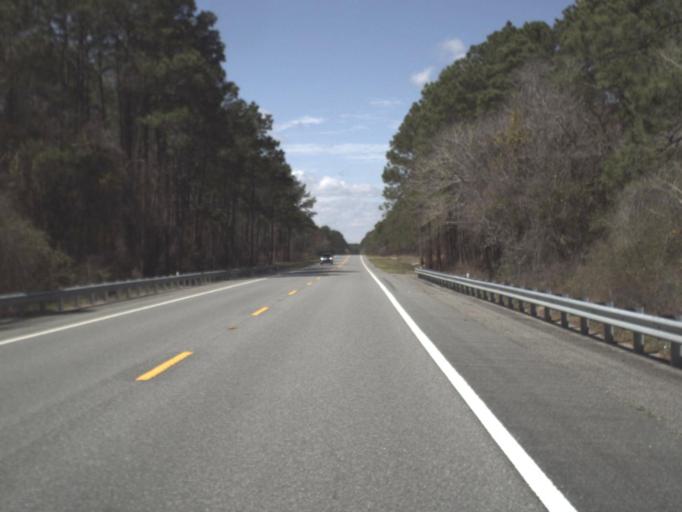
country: US
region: Florida
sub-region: Gadsden County
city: Midway
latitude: 30.3497
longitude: -84.5112
